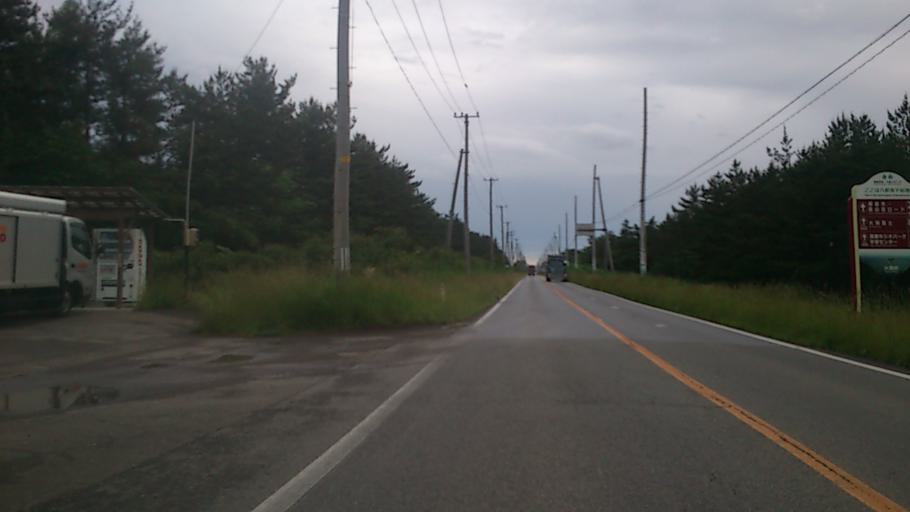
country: JP
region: Akita
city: Tenno
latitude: 40.0113
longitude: 139.9528
